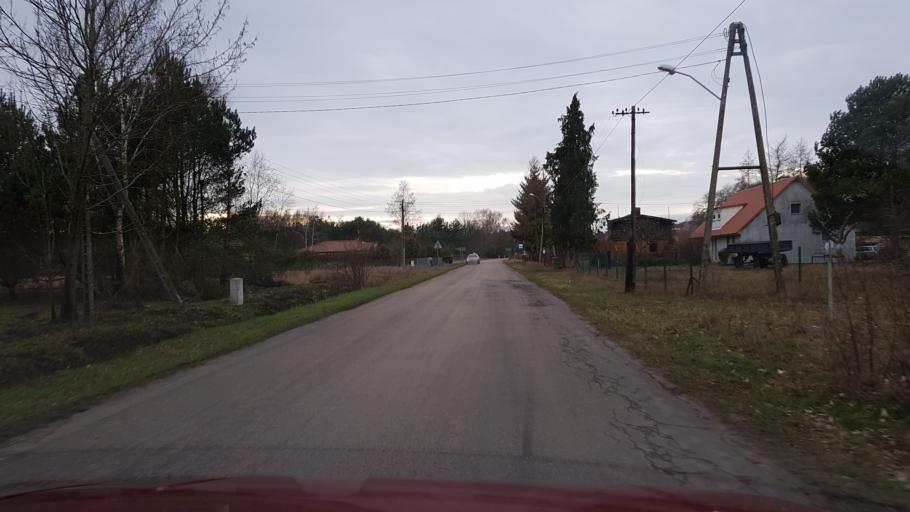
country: PL
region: West Pomeranian Voivodeship
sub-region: Powiat policki
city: Police
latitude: 53.5573
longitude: 14.4783
